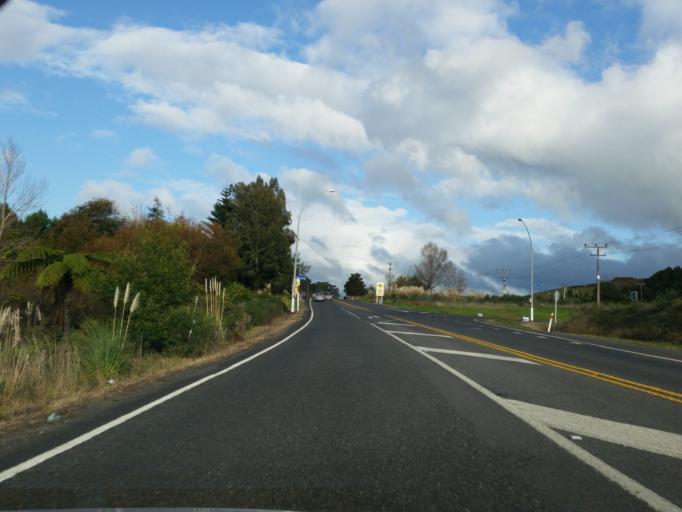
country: NZ
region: Bay of Plenty
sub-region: Western Bay of Plenty District
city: Katikati
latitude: -37.6474
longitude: 175.9664
